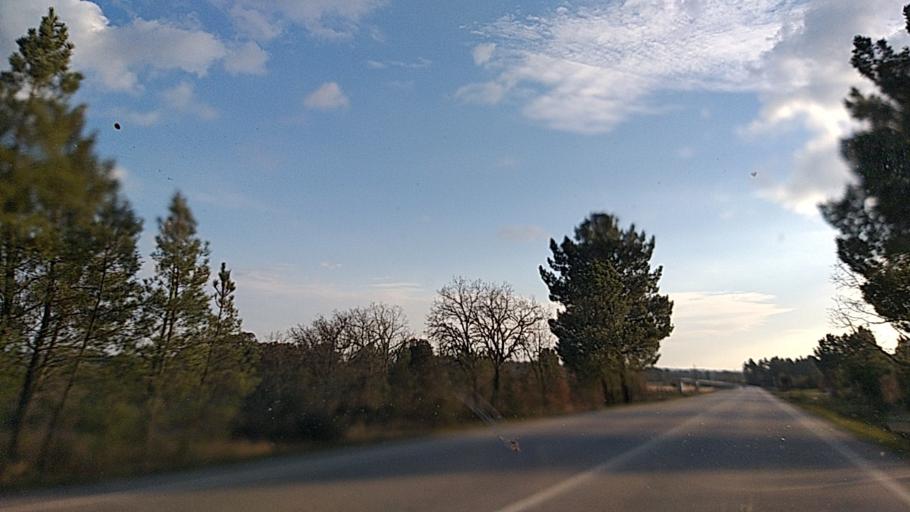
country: PT
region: Guarda
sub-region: Pinhel
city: Pinhel
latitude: 40.6409
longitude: -6.9703
